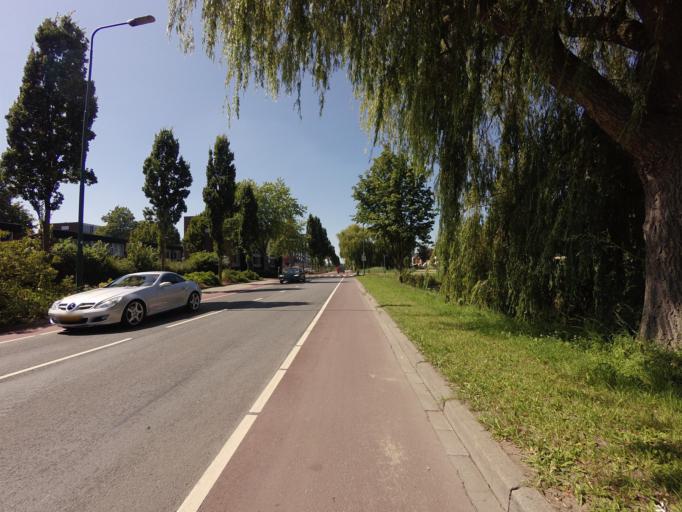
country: NL
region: Utrecht
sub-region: Stichtse Vecht
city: Maarssen
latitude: 52.1424
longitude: 5.0480
